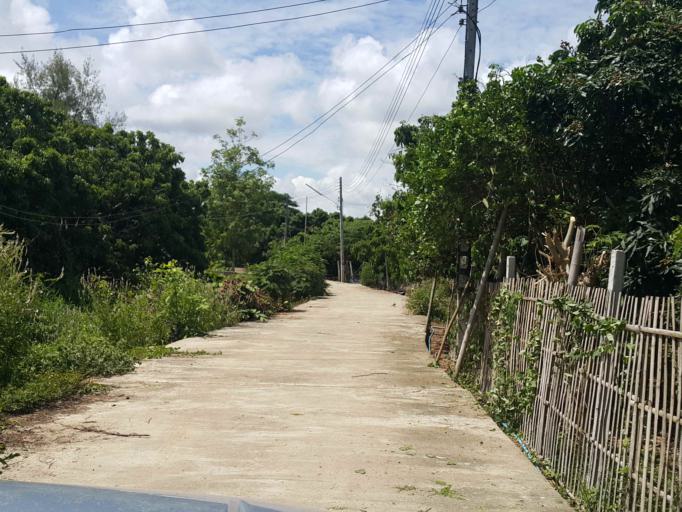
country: TH
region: Chiang Mai
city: Saraphi
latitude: 18.6917
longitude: 99.0197
